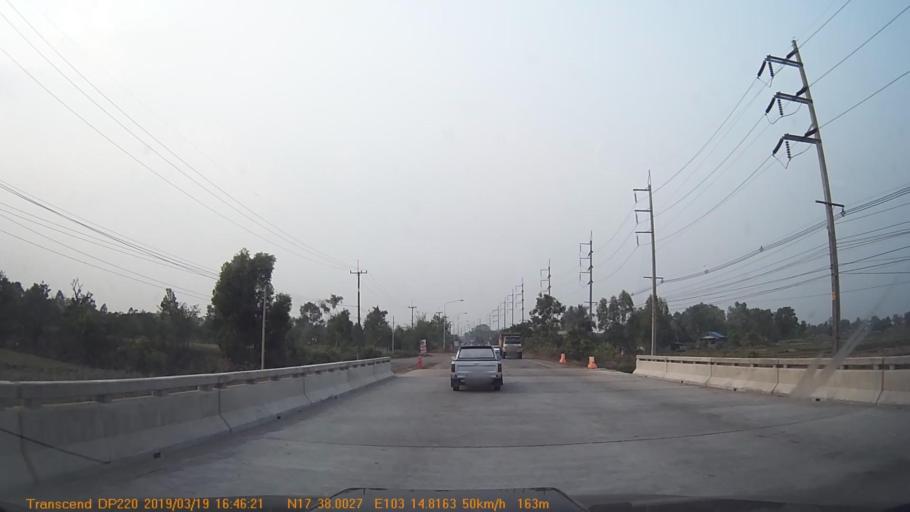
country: TH
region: Changwat Udon Thani
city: Ban Dung
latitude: 17.6337
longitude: 103.2468
